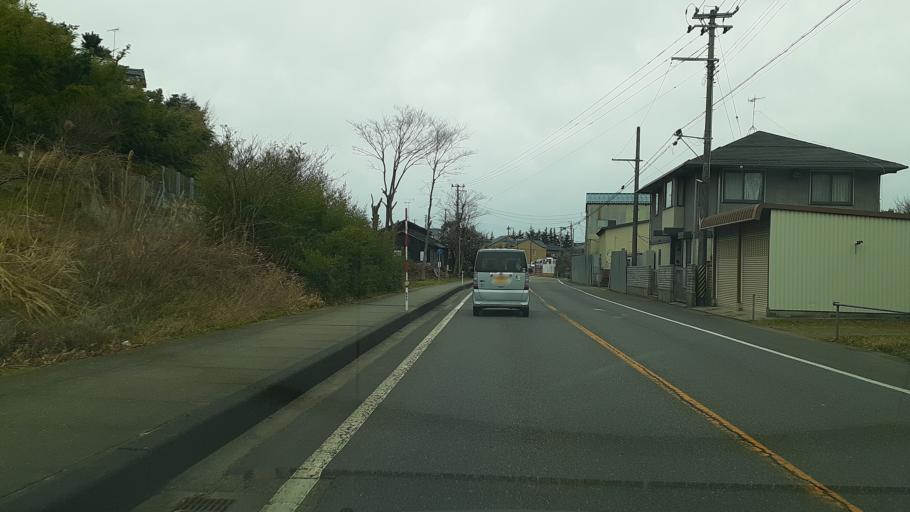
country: JP
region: Niigata
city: Niitsu-honcho
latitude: 37.7925
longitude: 139.1372
